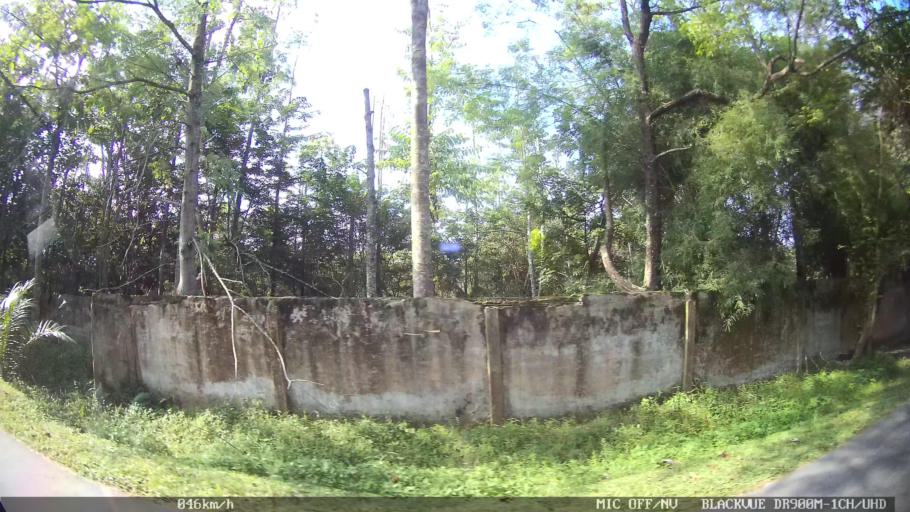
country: ID
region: North Sumatra
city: Percut
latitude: 3.5933
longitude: 98.8022
